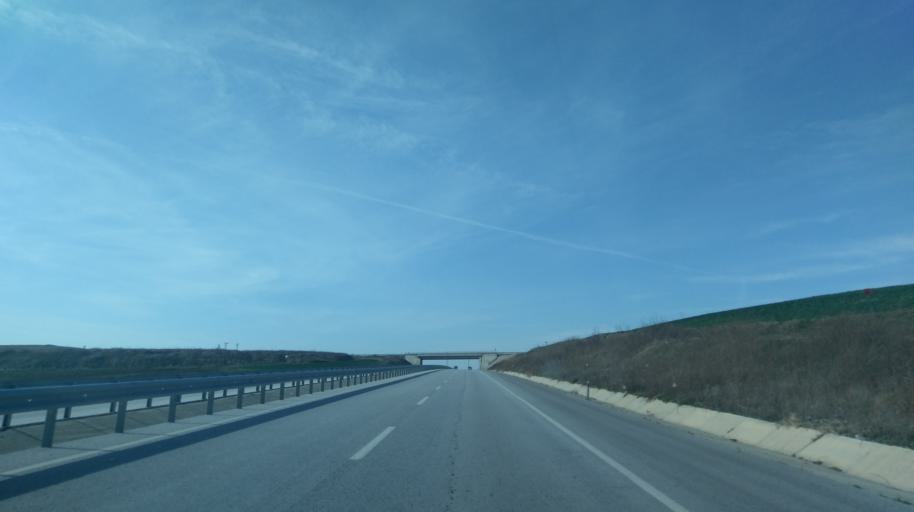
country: TR
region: Edirne
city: Uzun Keupru
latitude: 41.2423
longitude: 26.6943
